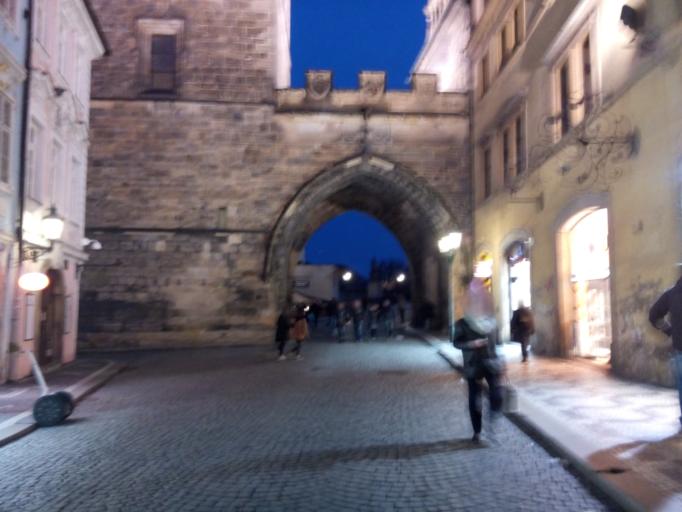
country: CZ
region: Praha
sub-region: Praha 1
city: Mala Strana
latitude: 50.0872
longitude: 14.4064
